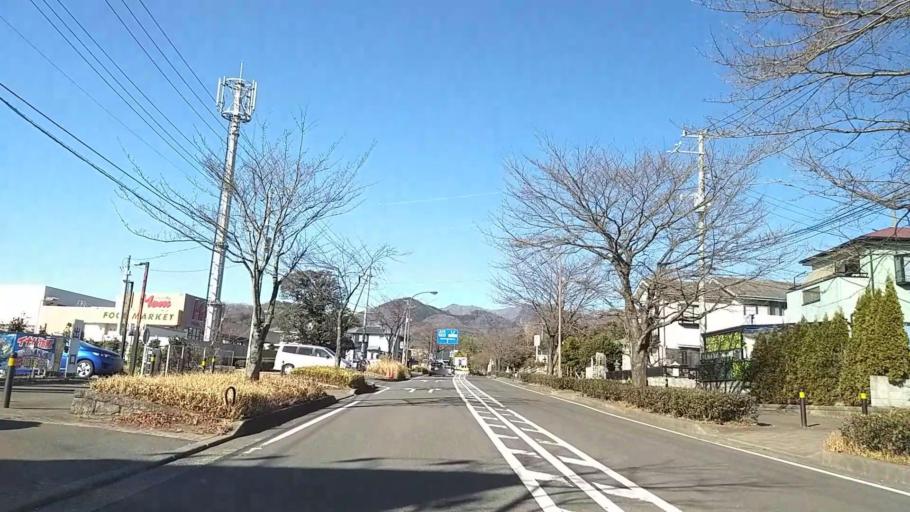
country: JP
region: Kanagawa
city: Hadano
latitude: 35.3872
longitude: 139.1796
